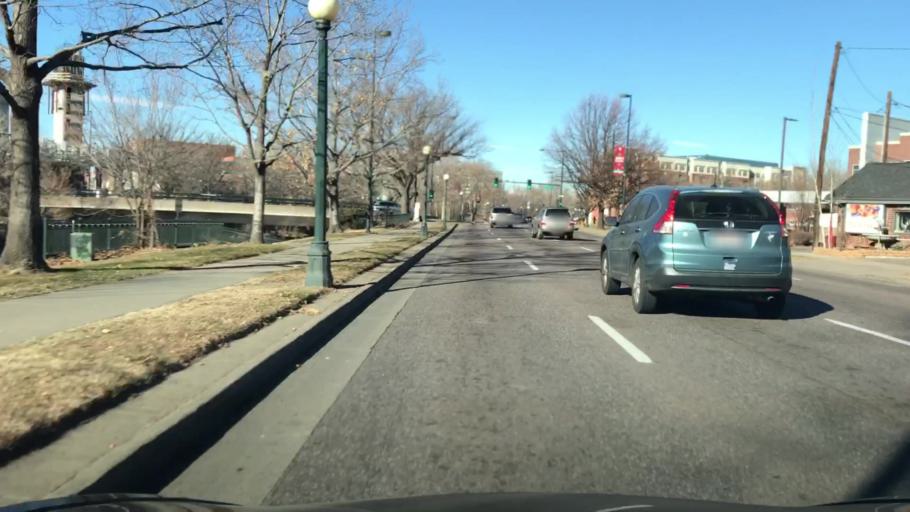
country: US
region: Colorado
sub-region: Denver County
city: Denver
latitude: 39.7226
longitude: -104.9816
